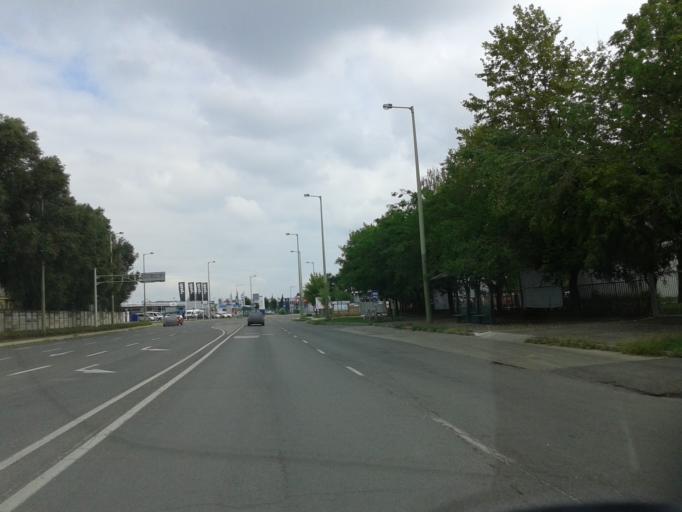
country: HU
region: Csongrad
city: Szeged
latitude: 46.2538
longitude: 20.1238
